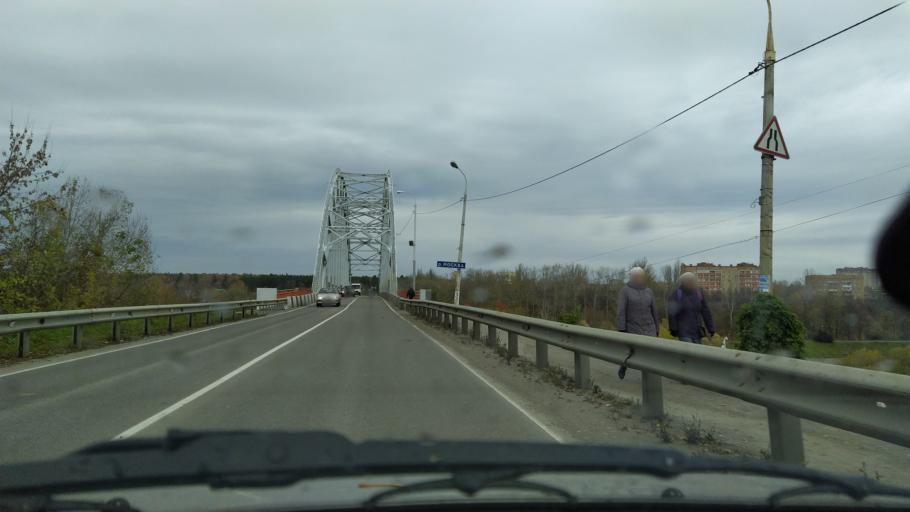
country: RU
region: Moskovskaya
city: Voskresensk
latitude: 55.3200
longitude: 38.6512
